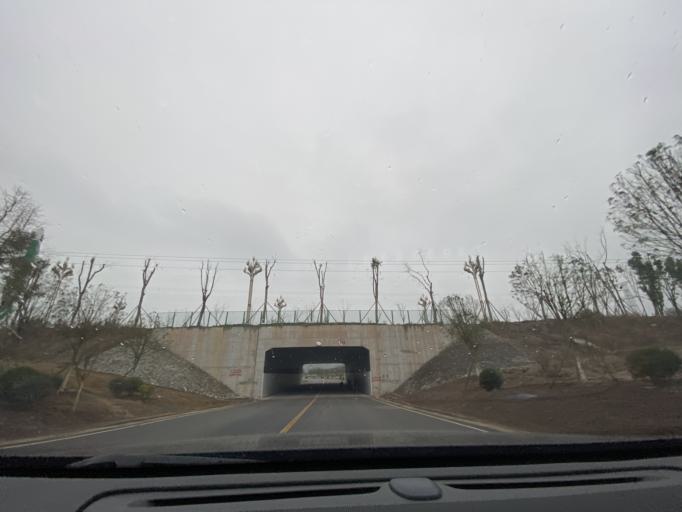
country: CN
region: Sichuan
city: Jiancheng
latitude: 30.3944
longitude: 104.6339
